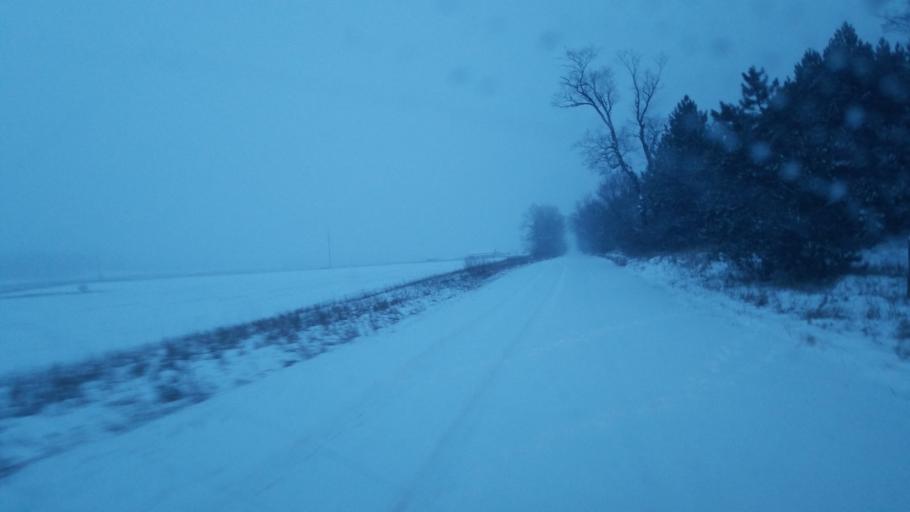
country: US
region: Michigan
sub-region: Osceola County
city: Reed City
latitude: 43.8398
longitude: -85.4141
